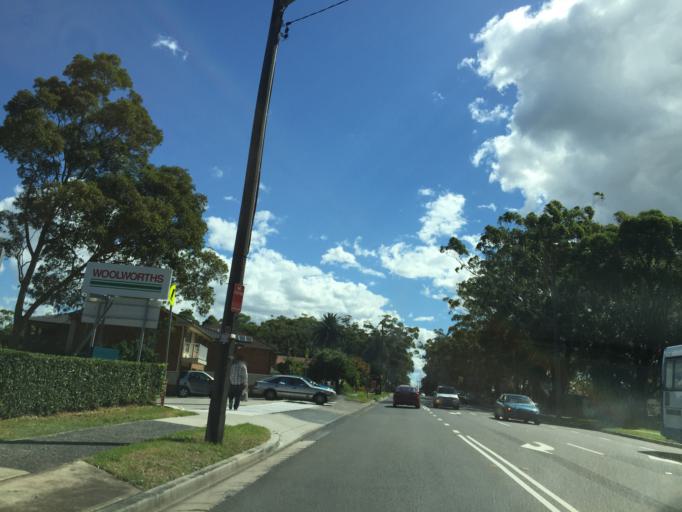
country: AU
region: New South Wales
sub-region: Ryde
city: Marsfield
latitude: -33.7781
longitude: 151.1074
